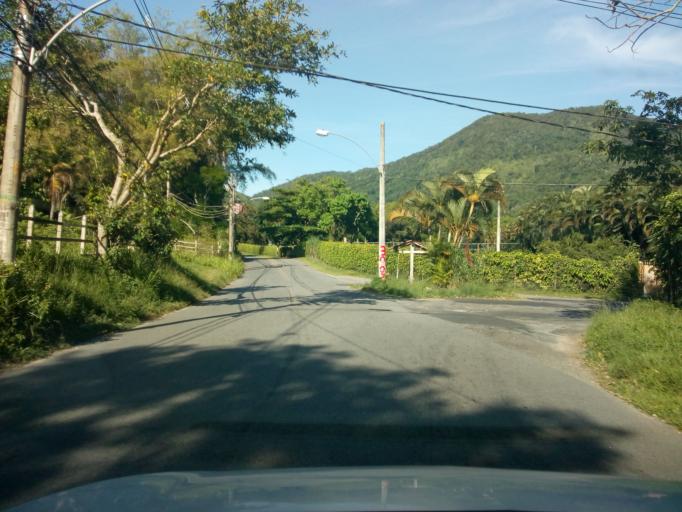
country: BR
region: Rio de Janeiro
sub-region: Nilopolis
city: Nilopolis
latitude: -23.0256
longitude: -43.5136
